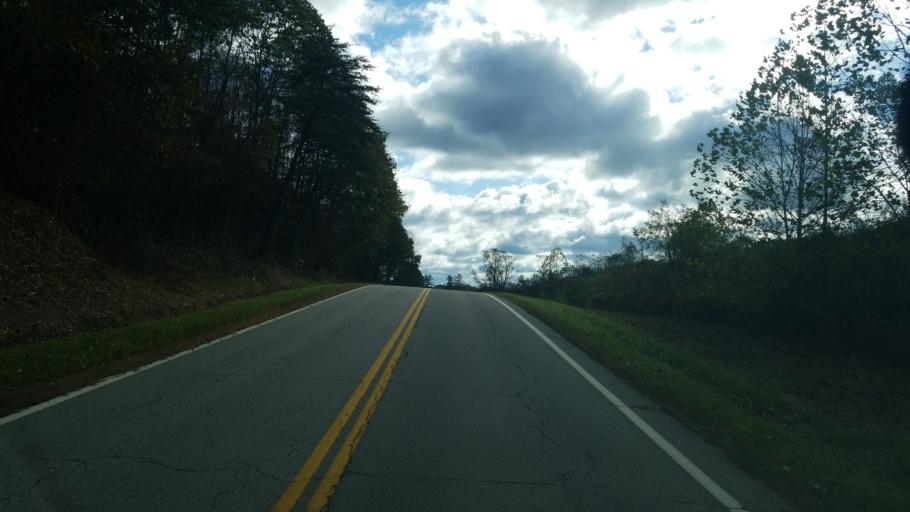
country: US
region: Ohio
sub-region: Vinton County
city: McArthur
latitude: 39.1637
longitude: -82.4463
